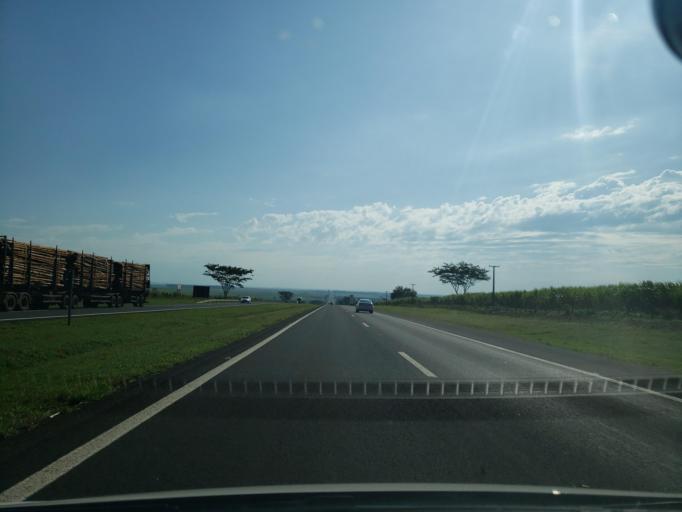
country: BR
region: Sao Paulo
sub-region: Penapolis
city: Penapolis
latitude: -21.5094
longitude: -50.0203
